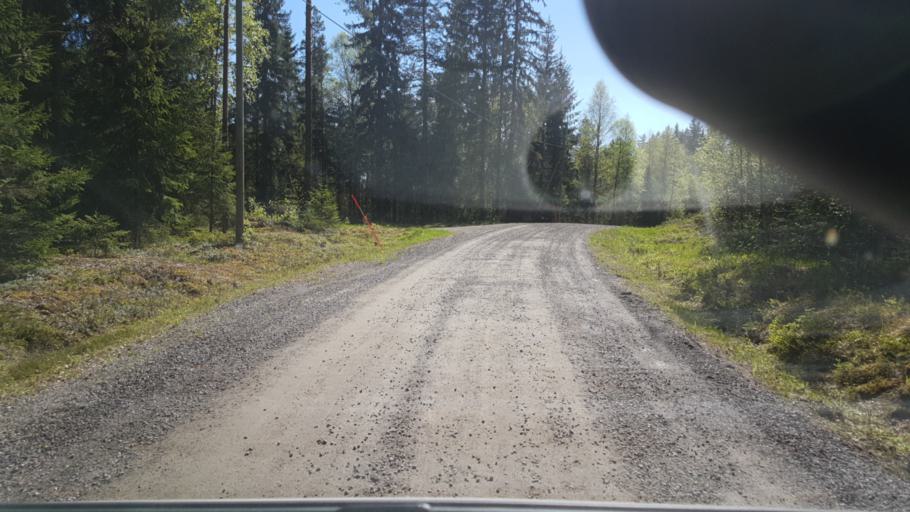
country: SE
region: Vaermland
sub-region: Eda Kommun
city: Charlottenberg
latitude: 59.9119
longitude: 12.3852
